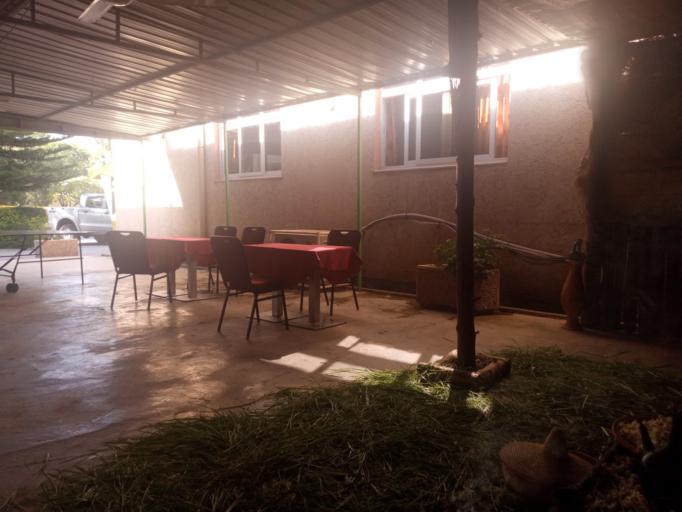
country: ET
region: Oromiya
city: Ziway
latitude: 7.9272
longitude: 38.7230
